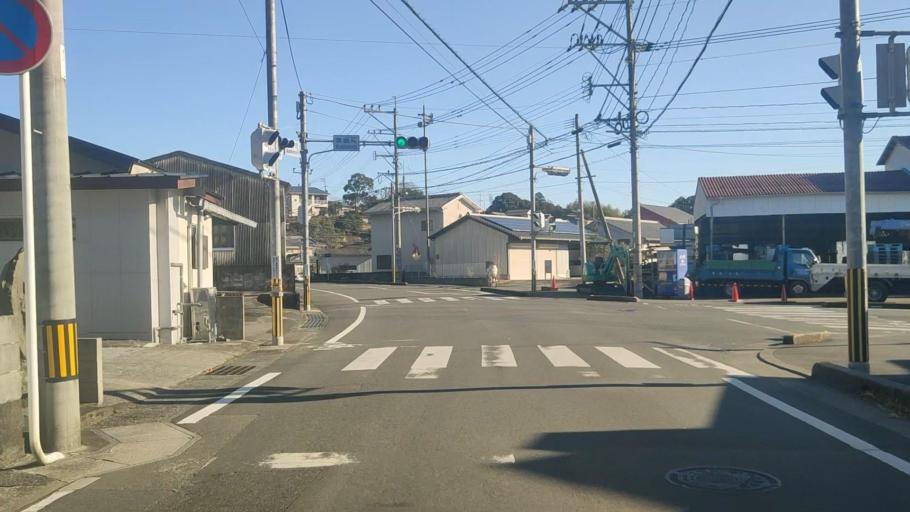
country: JP
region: Miyazaki
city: Nobeoka
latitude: 32.6096
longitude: 131.6879
